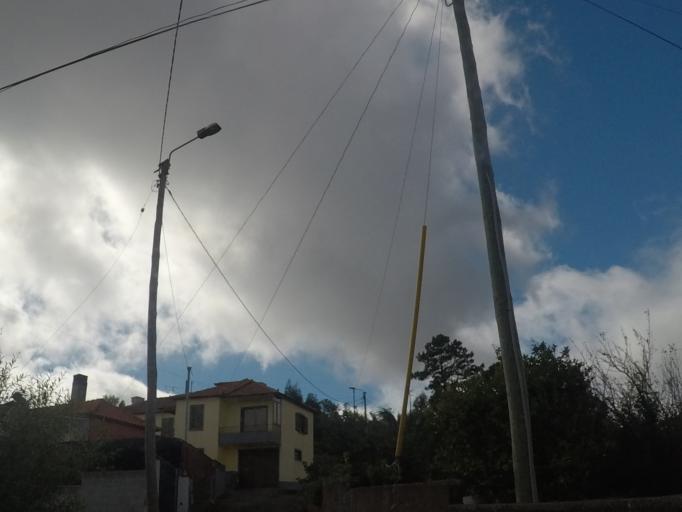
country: PT
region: Madeira
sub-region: Santa Cruz
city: Camacha
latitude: 32.6840
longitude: -16.8538
